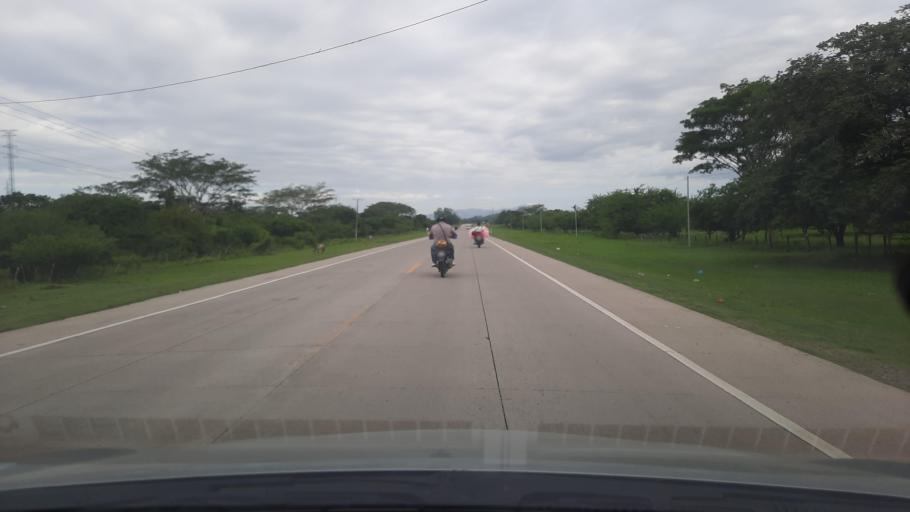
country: NI
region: Chinandega
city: Somotillo
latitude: 12.8960
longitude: -86.8509
